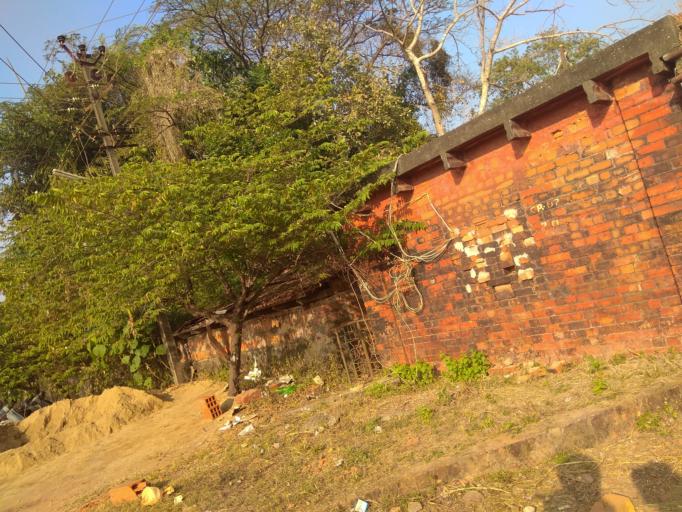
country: IN
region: Karnataka
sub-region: Dakshina Kannada
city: Ullal
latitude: 12.8447
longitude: 74.8533
